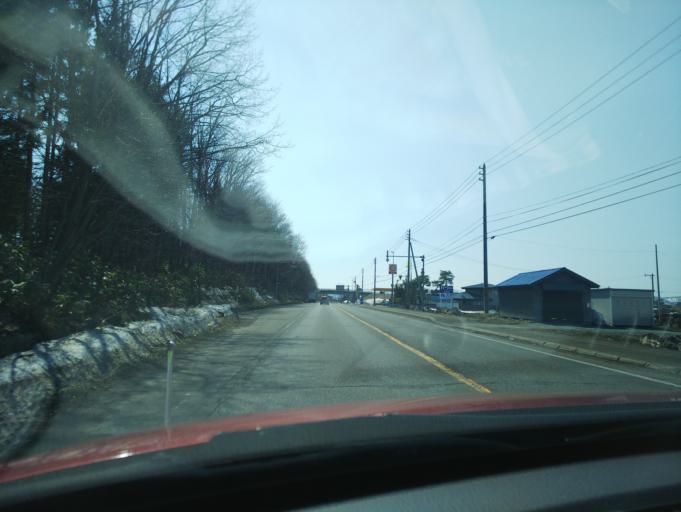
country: JP
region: Hokkaido
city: Nayoro
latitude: 44.3016
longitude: 142.4318
